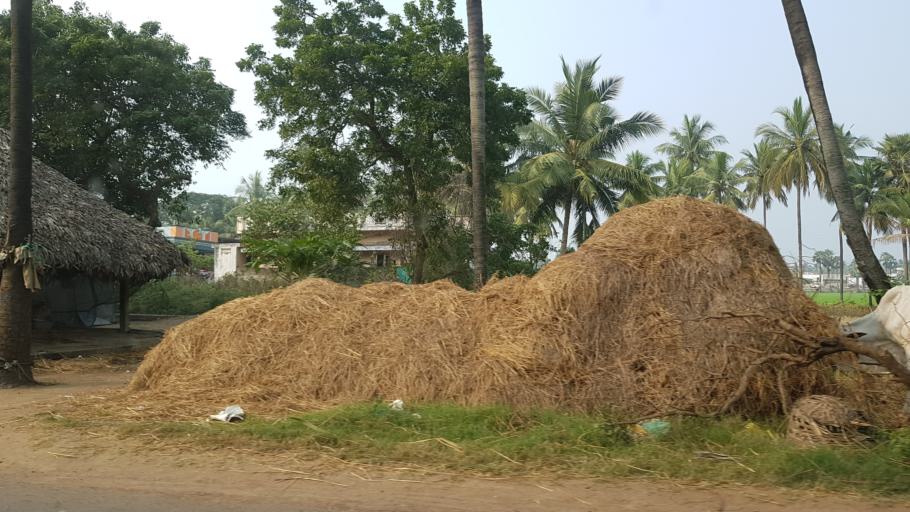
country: IN
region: Andhra Pradesh
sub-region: West Godavari
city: Akividu
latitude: 16.5354
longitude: 81.4017
